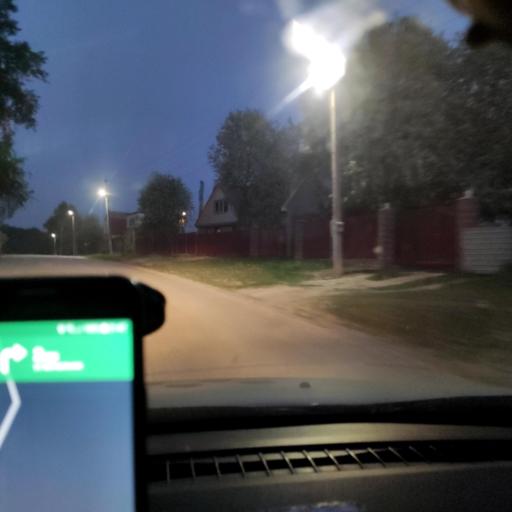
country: RU
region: Bashkortostan
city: Kabakovo
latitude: 54.6683
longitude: 56.2793
